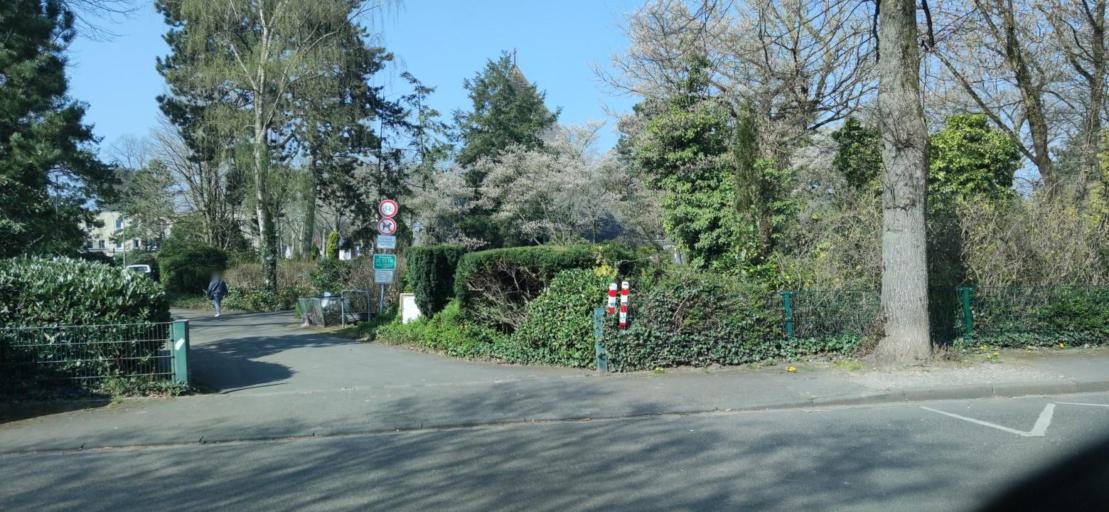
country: DE
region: North Rhine-Westphalia
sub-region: Regierungsbezirk Dusseldorf
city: Kaarst
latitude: 51.2004
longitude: 6.6067
